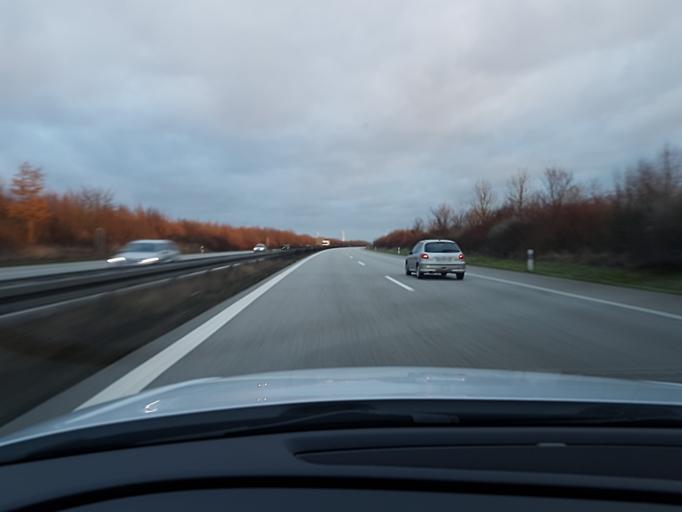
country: DE
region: Mecklenburg-Vorpommern
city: Grevesmuhlen
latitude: 53.8314
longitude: 11.2137
